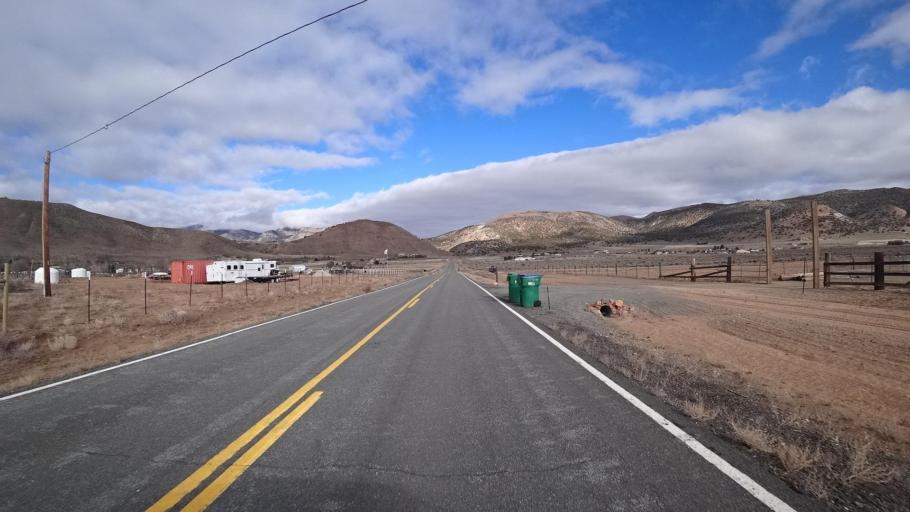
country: US
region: Nevada
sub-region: Washoe County
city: Cold Springs
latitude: 39.8919
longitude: -119.9768
